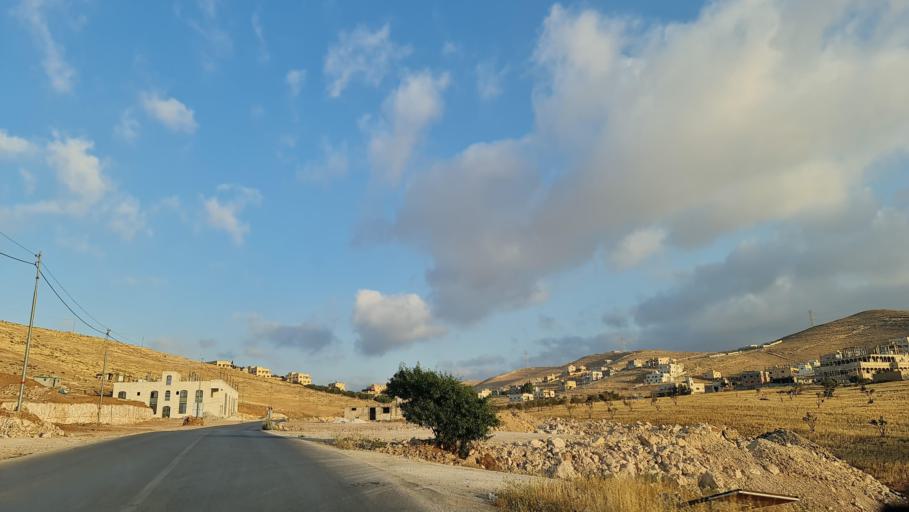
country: JO
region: Zarqa
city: Zarqa
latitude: 32.0844
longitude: 36.0293
